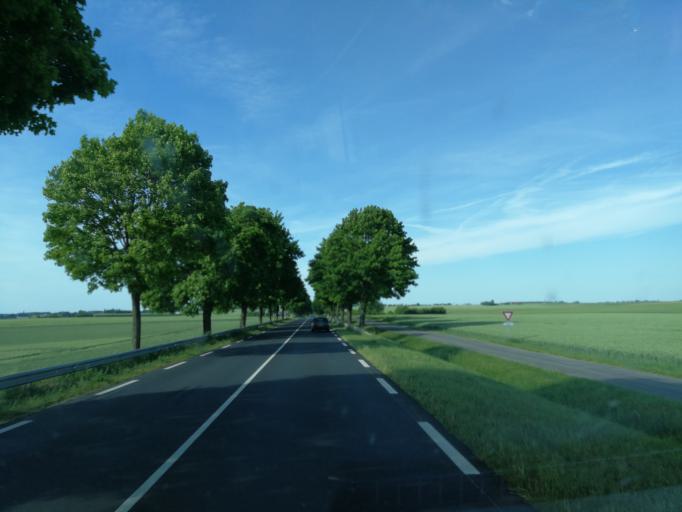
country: FR
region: Centre
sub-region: Departement du Loir-et-Cher
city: Naveil
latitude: 47.7395
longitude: 1.0342
